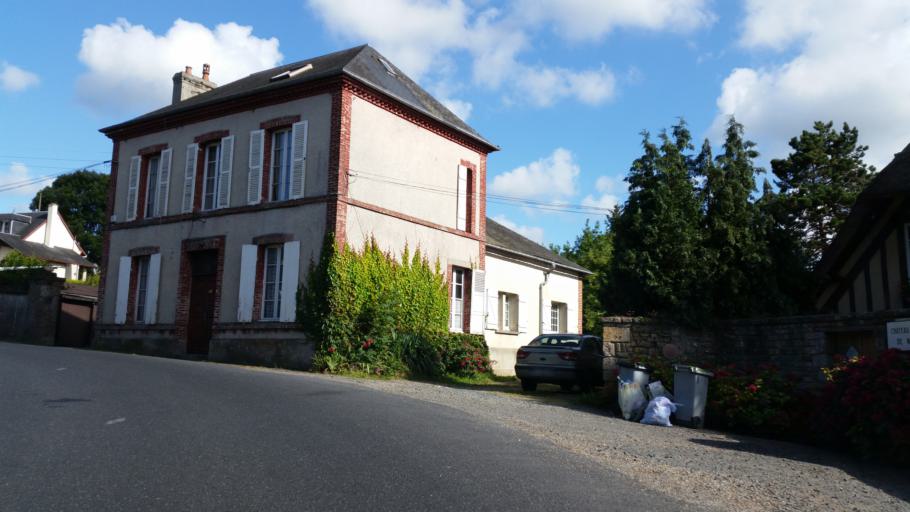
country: FR
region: Lower Normandy
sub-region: Departement du Calvados
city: Touques
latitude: 49.3379
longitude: 0.1182
